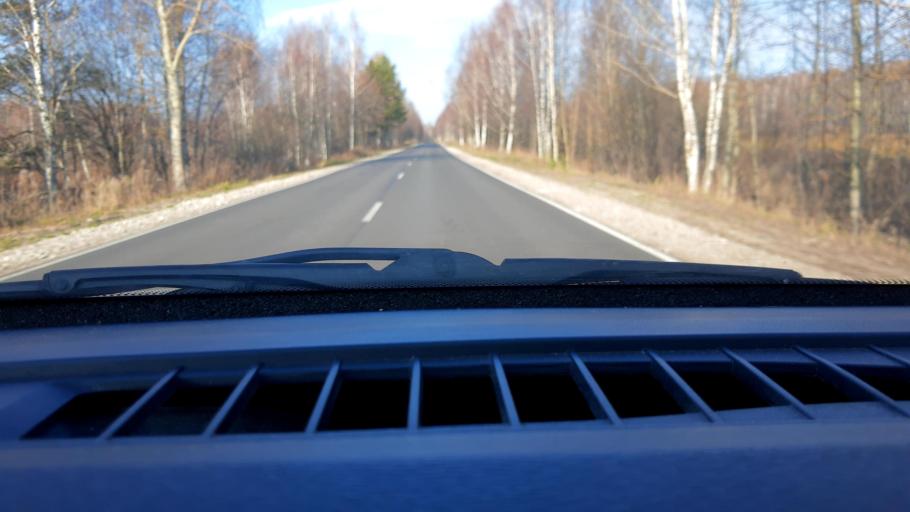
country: RU
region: Nizjnij Novgorod
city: Neklyudovo
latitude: 56.4953
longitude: 43.8561
